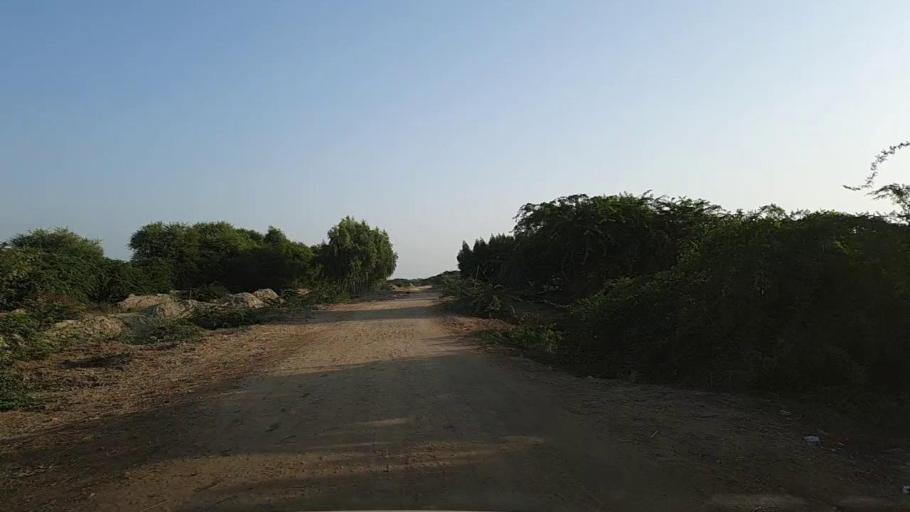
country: PK
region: Sindh
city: Kario
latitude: 24.7135
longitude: 68.6670
